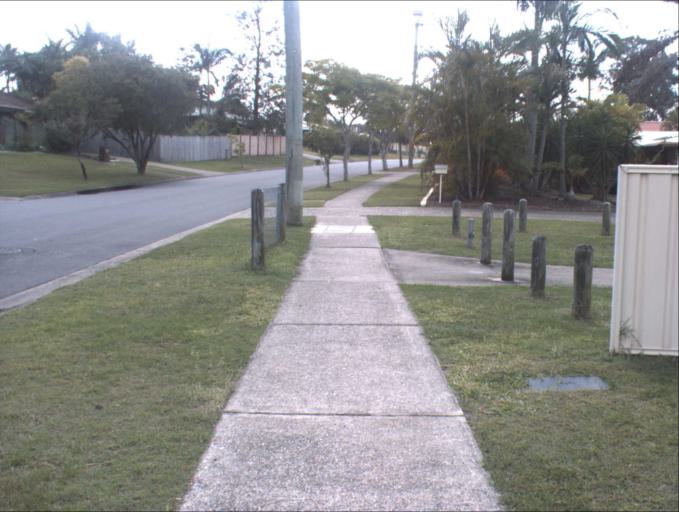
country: AU
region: Queensland
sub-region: Logan
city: Park Ridge South
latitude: -27.6747
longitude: 153.0361
